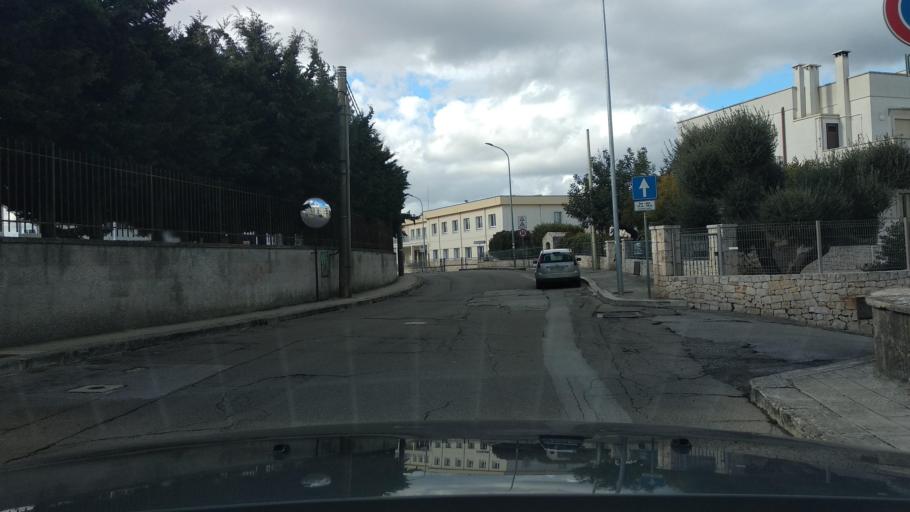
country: IT
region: Apulia
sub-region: Provincia di Brindisi
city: Cisternino
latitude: 40.7443
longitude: 17.4209
